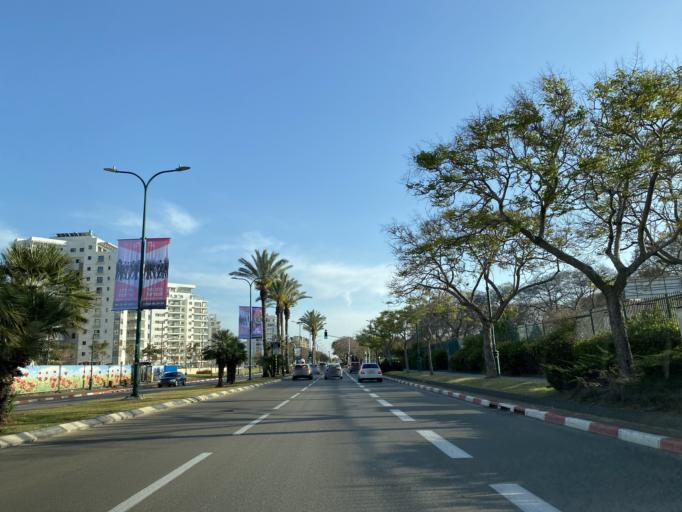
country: IL
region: Tel Aviv
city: Herzliyya
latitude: 32.1677
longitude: 34.8283
